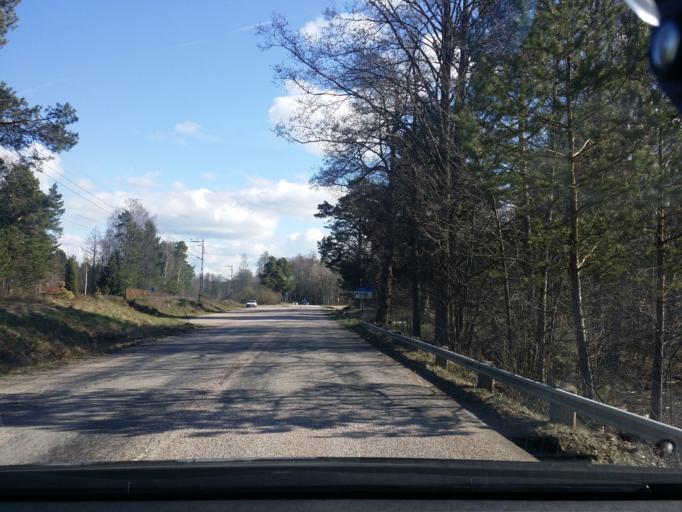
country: SE
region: Vaestmanland
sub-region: Sala Kommun
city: Sala
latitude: 59.9568
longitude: 16.5165
